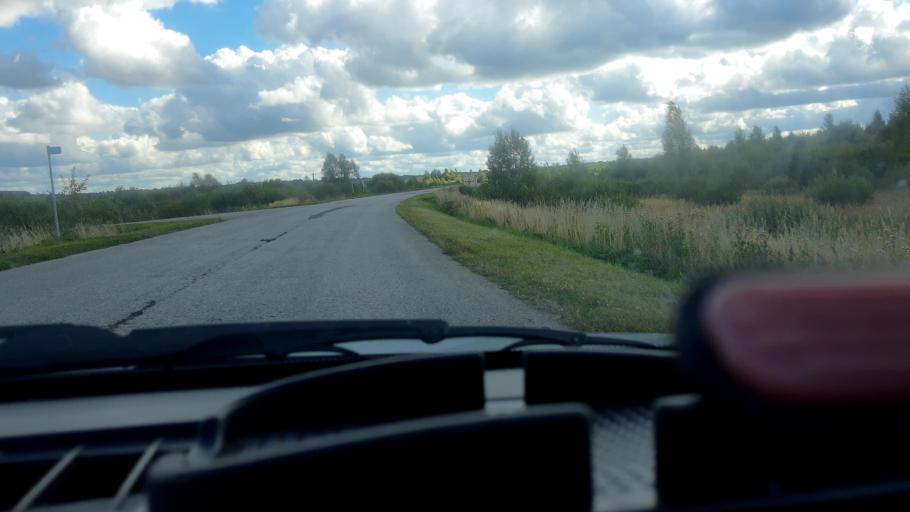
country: RU
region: Mariy-El
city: Kilemary
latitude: 56.9417
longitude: 46.6853
